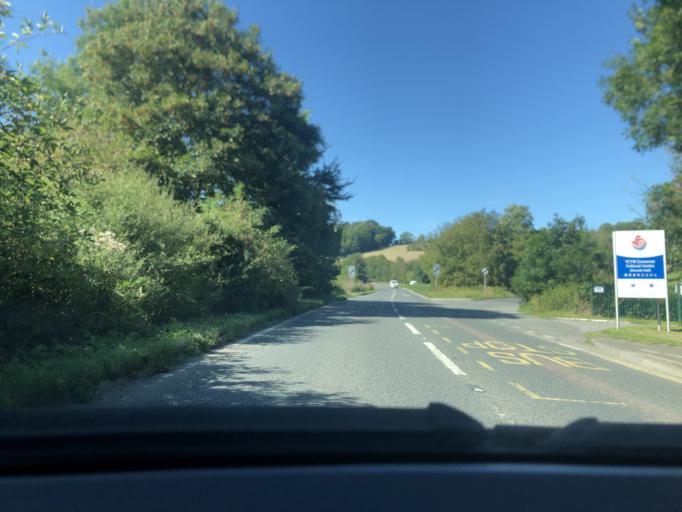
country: GB
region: England
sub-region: Somerset
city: Puriton
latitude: 51.1578
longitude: -2.9617
